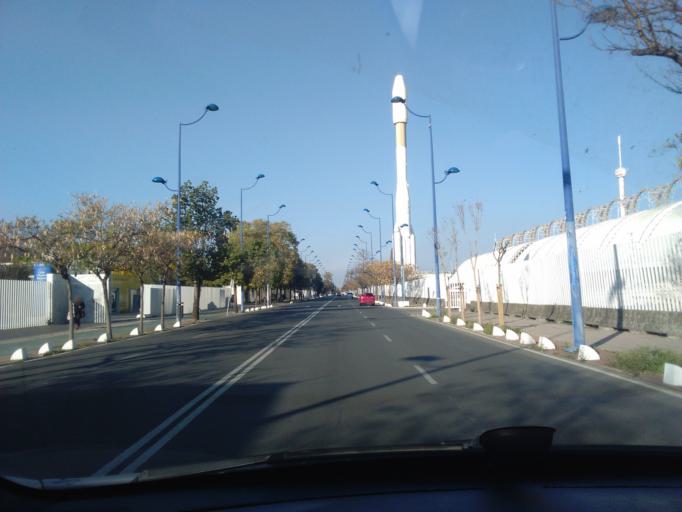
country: ES
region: Andalusia
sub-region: Provincia de Sevilla
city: Camas
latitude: 37.4013
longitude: -6.0043
